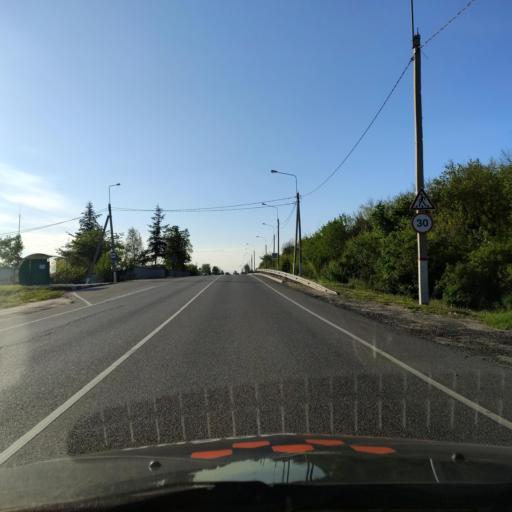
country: RU
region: Lipetsk
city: Yelets
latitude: 52.5587
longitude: 38.6917
